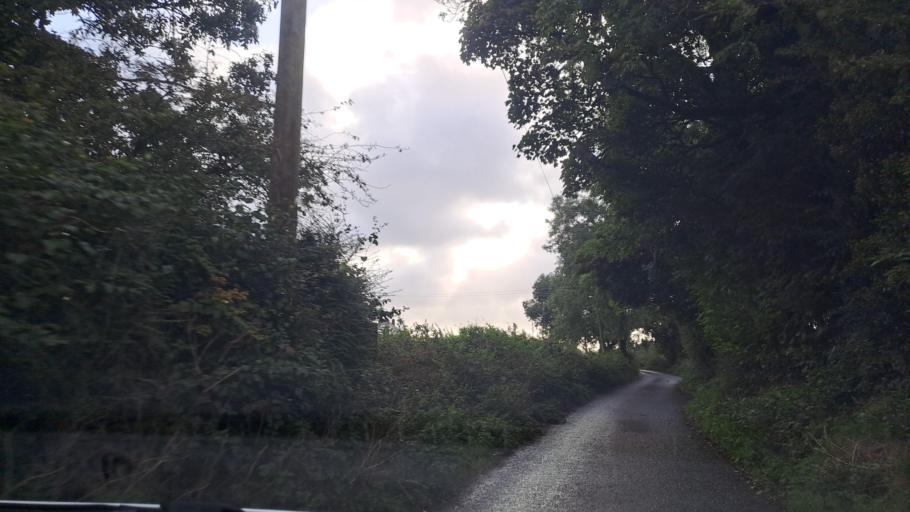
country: IE
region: Ulster
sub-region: An Cabhan
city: Kingscourt
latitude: 53.9673
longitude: -6.8409
